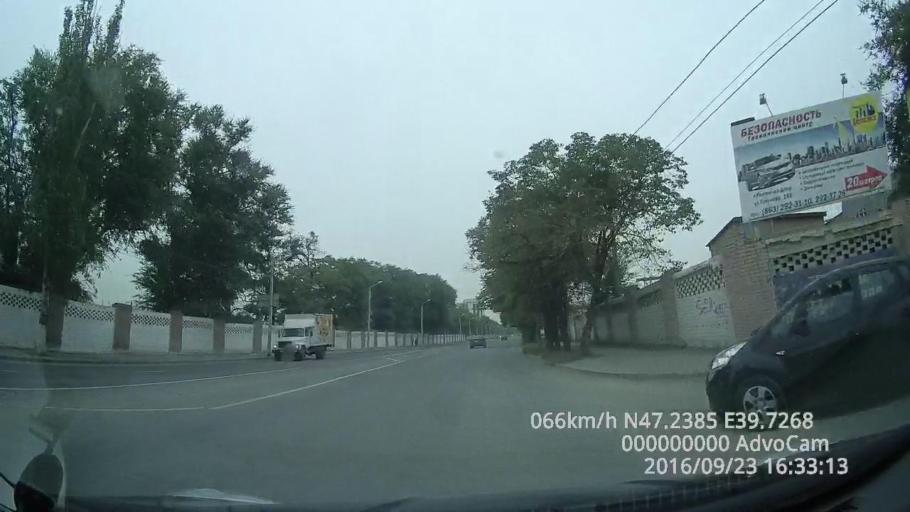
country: RU
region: Rostov
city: Rostov-na-Donu
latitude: 47.2384
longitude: 39.7263
